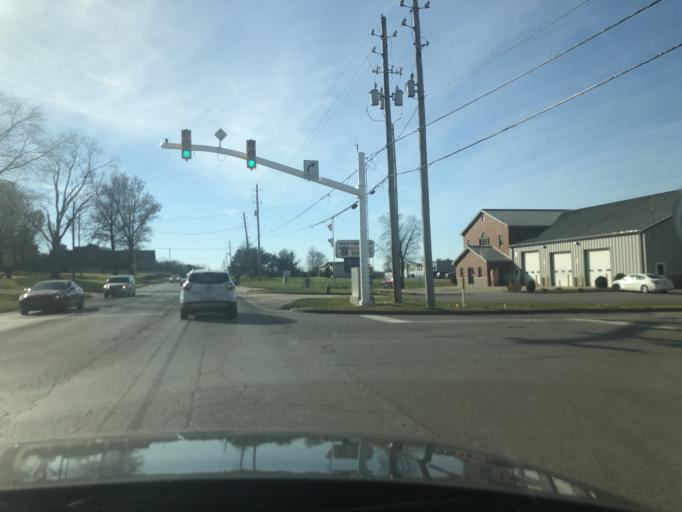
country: US
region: Indiana
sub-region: Warrick County
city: Newburgh
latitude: 37.9734
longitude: -87.4412
